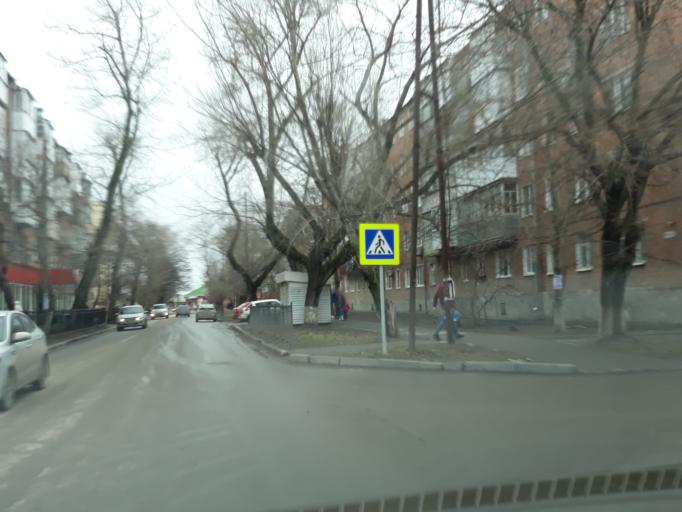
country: RU
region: Rostov
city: Taganrog
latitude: 47.2086
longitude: 38.8940
